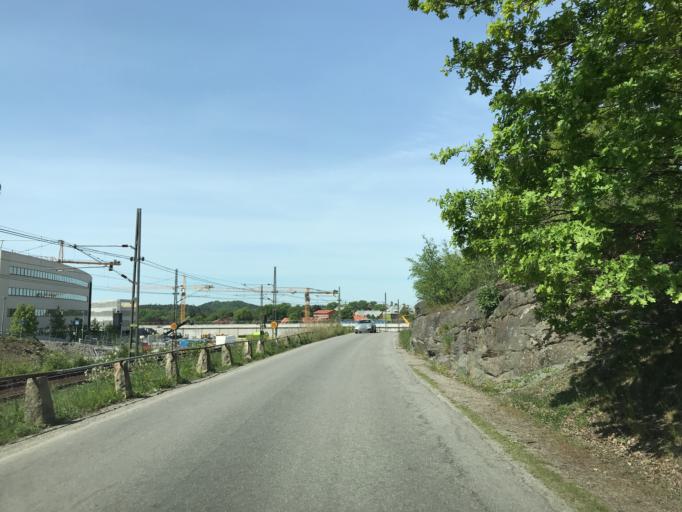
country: SE
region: Stockholm
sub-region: Stockholms Kommun
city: Stockholm
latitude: 59.3532
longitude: 18.0617
